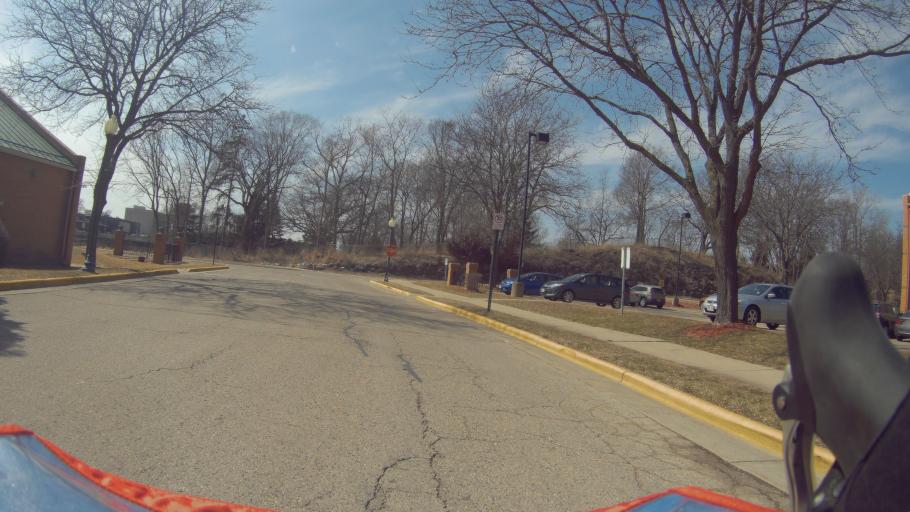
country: US
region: Wisconsin
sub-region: Dane County
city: Shorewood Hills
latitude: 43.0758
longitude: -89.4381
